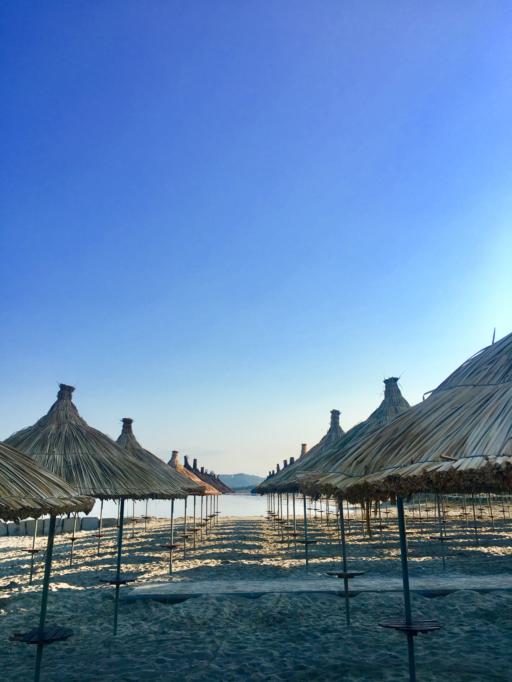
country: AL
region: Tirane
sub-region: Rrethi i Kavajes
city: Golem
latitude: 41.2475
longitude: 19.5201
